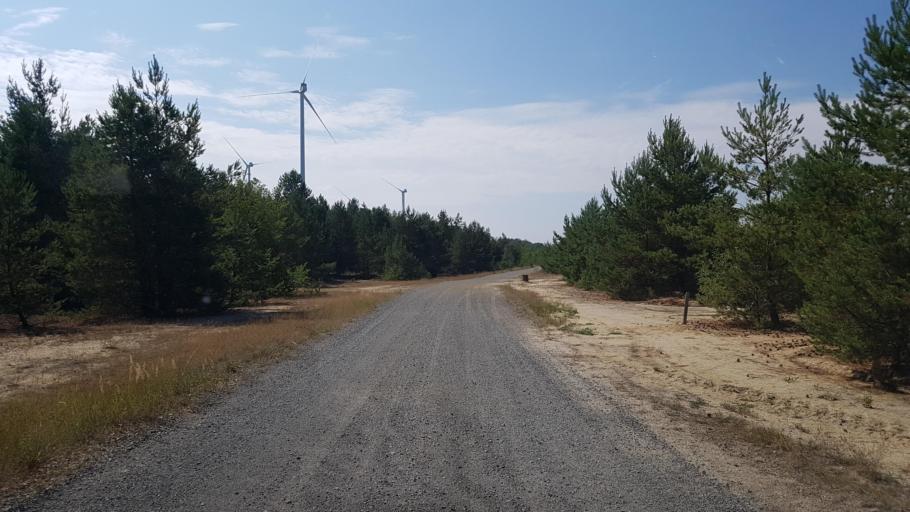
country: DE
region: Brandenburg
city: Schipkau
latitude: 51.5371
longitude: 13.8627
